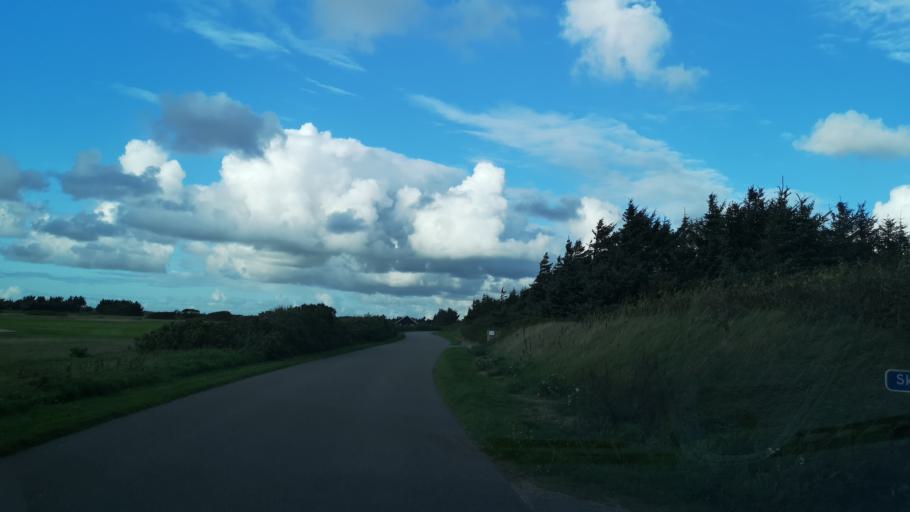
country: DK
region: Central Jutland
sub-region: Ringkobing-Skjern Kommune
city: Ringkobing
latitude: 56.1267
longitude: 8.1288
